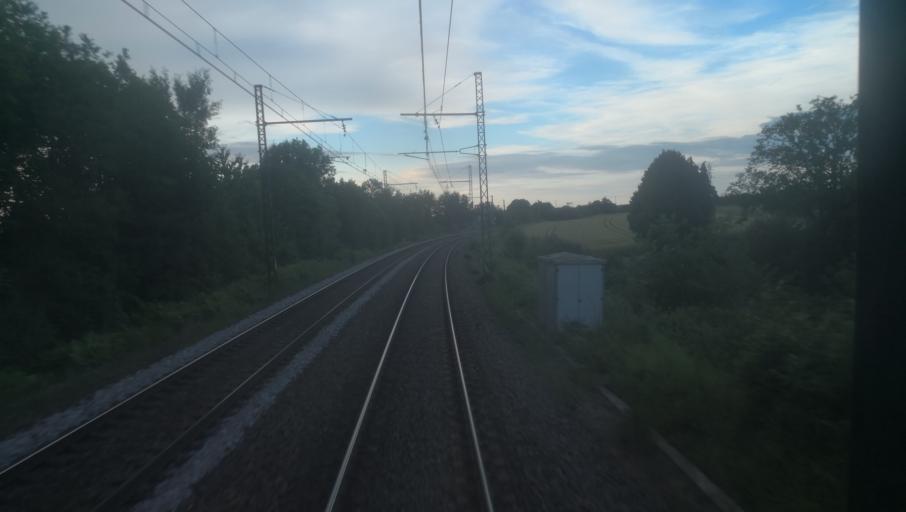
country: FR
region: Limousin
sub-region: Departement de la Creuse
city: Saint-Maurice-la-Souterraine
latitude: 46.1605
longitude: 1.4200
